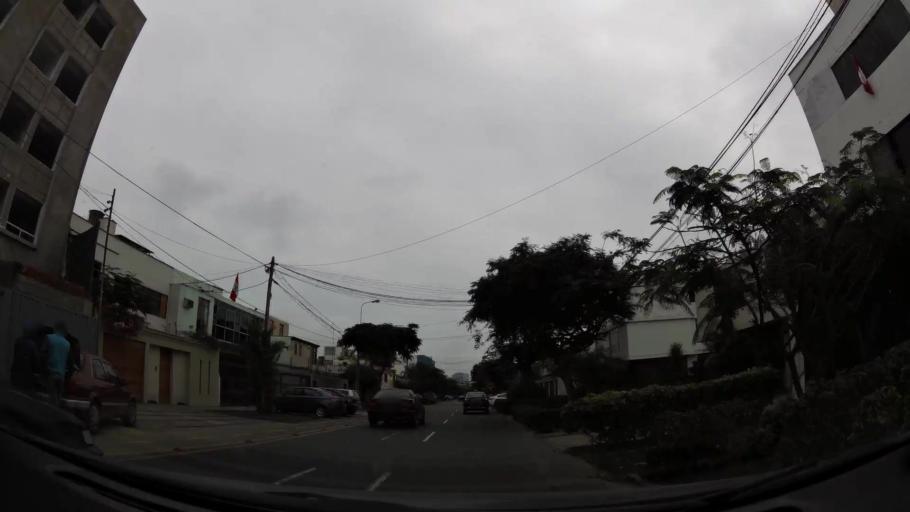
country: PE
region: Lima
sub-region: Lima
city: San Isidro
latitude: -12.0904
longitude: -77.0435
